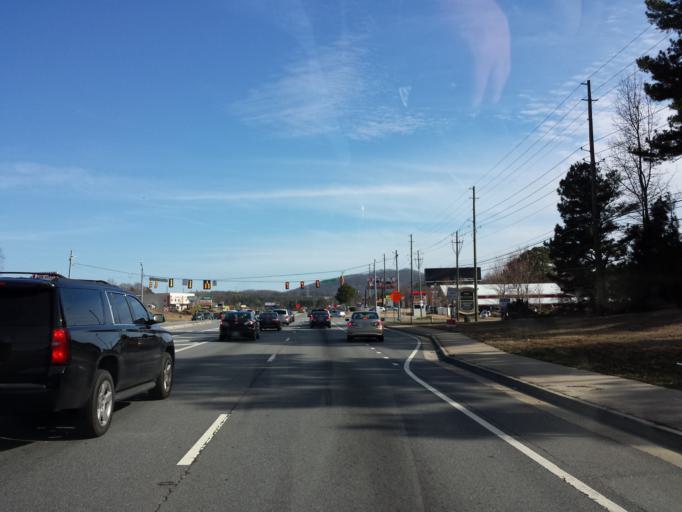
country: US
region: Georgia
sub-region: Cobb County
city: Kennesaw
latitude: 34.0078
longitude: -84.6067
